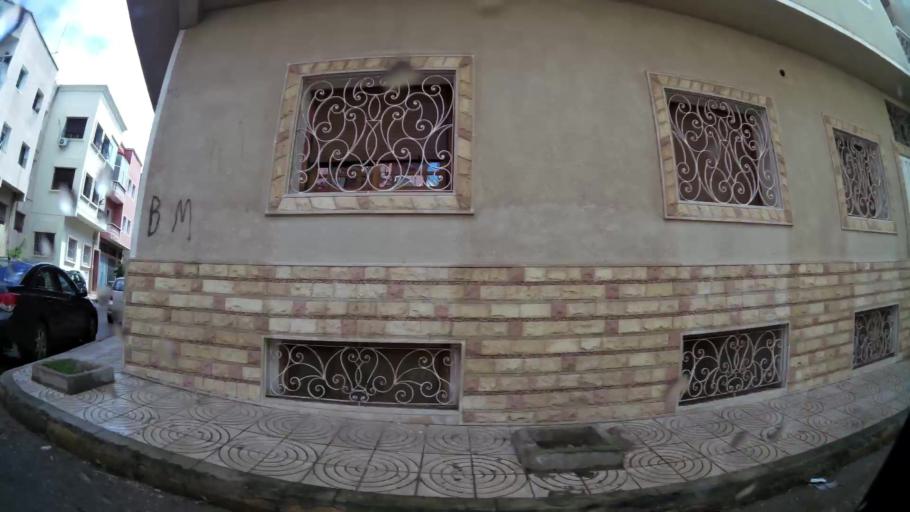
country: MA
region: Grand Casablanca
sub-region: Casablanca
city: Casablanca
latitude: 33.5312
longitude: -7.6529
